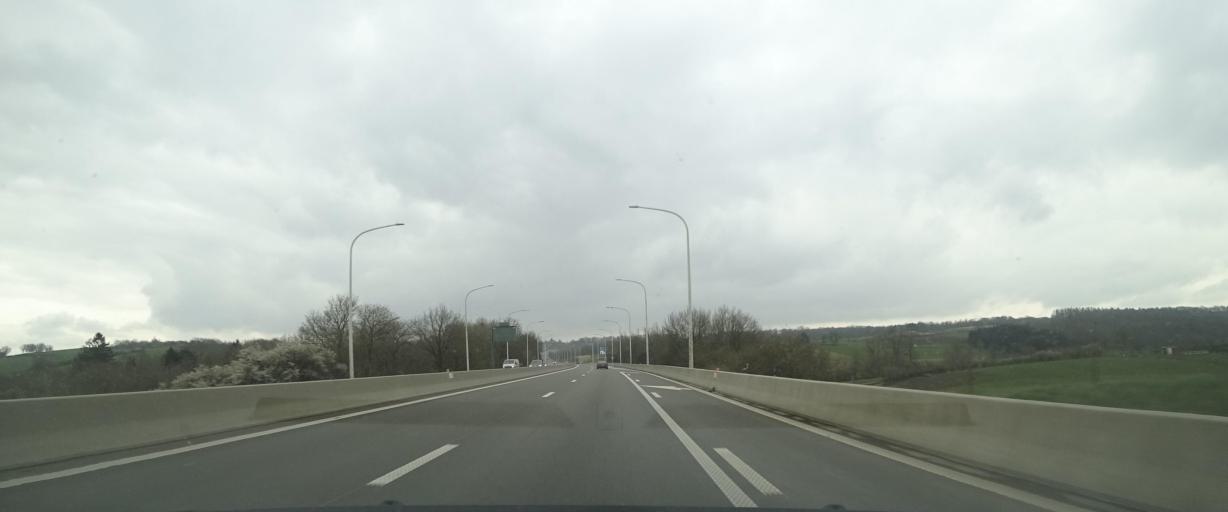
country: BE
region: Wallonia
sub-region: Province du Luxembourg
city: Marche-en-Famenne
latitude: 50.2667
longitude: 5.2475
